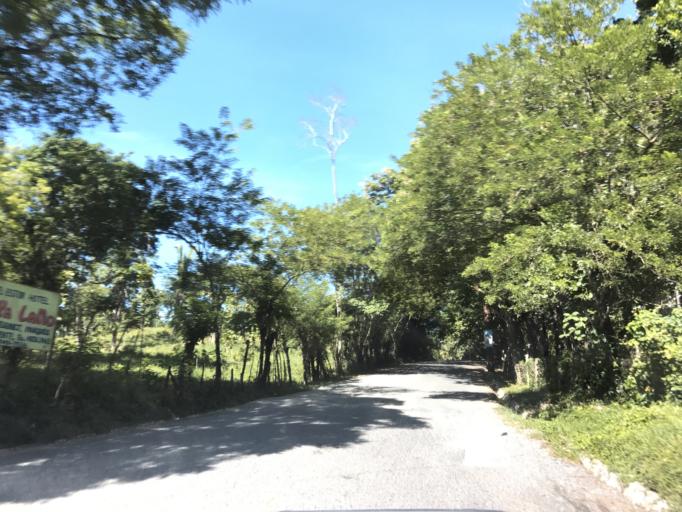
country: GT
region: Izabal
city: Morales
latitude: 15.6488
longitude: -89.0088
